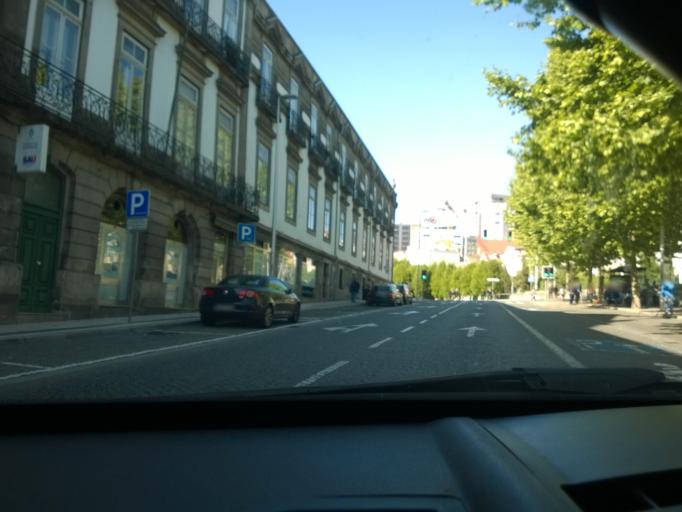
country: PT
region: Porto
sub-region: Porto
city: Porto
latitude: 41.1510
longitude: -8.6099
